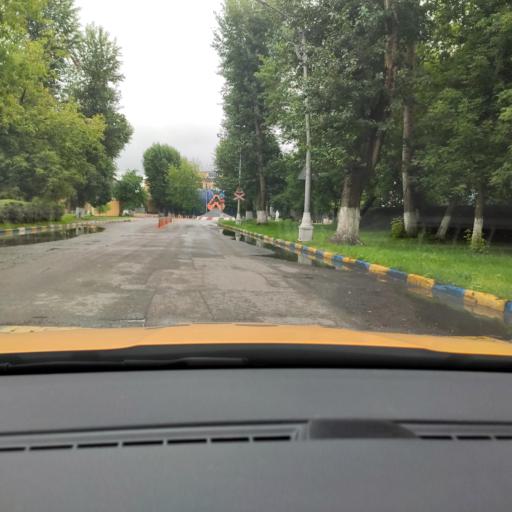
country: RU
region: Moskovskaya
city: Kozhukhovo
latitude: 55.6991
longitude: 37.6959
